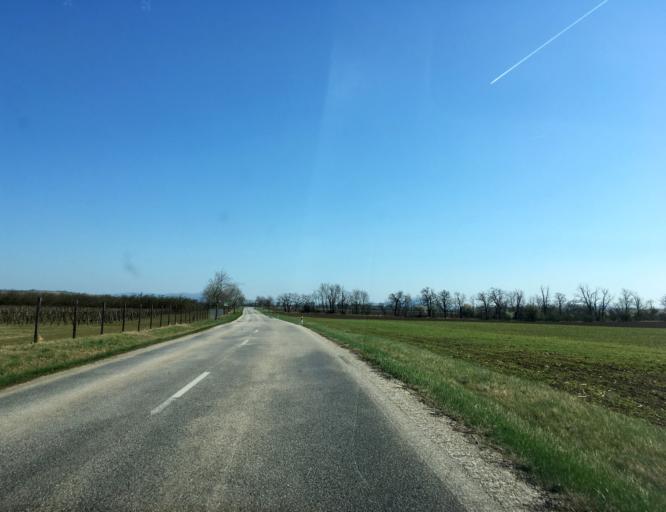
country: HU
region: Komarom-Esztergom
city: Nyergesujfalu
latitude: 47.8349
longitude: 18.5439
